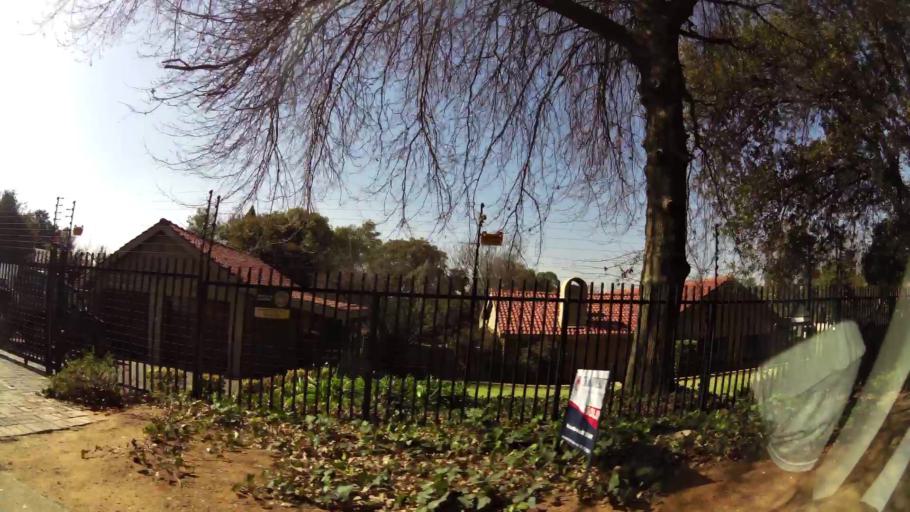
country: ZA
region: Gauteng
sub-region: City of Johannesburg Metropolitan Municipality
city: Modderfontein
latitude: -26.1625
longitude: 28.1284
